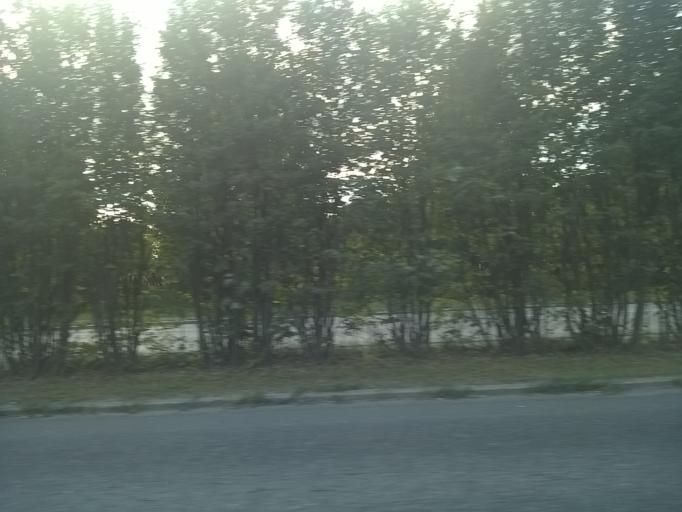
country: FI
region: Pirkanmaa
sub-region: Tampere
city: Tampere
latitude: 61.4866
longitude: 23.7786
